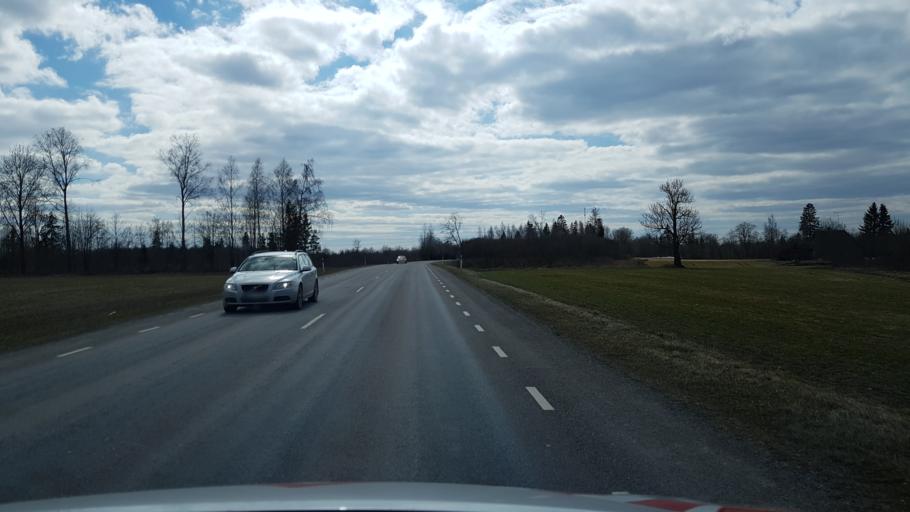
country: EE
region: Laeaene-Virumaa
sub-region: Vaeike-Maarja vald
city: Vaike-Maarja
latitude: 59.1499
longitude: 26.2636
